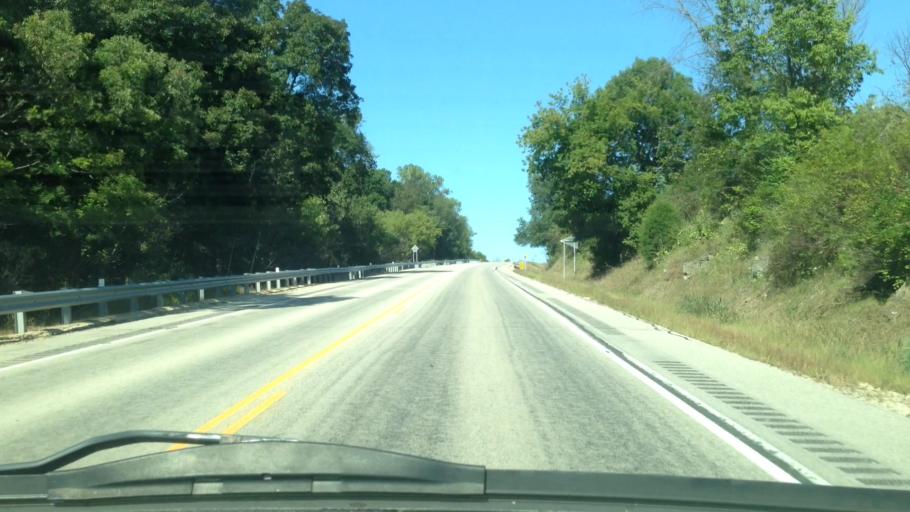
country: US
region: Minnesota
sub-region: Fillmore County
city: Rushford
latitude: 43.8492
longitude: -91.7505
